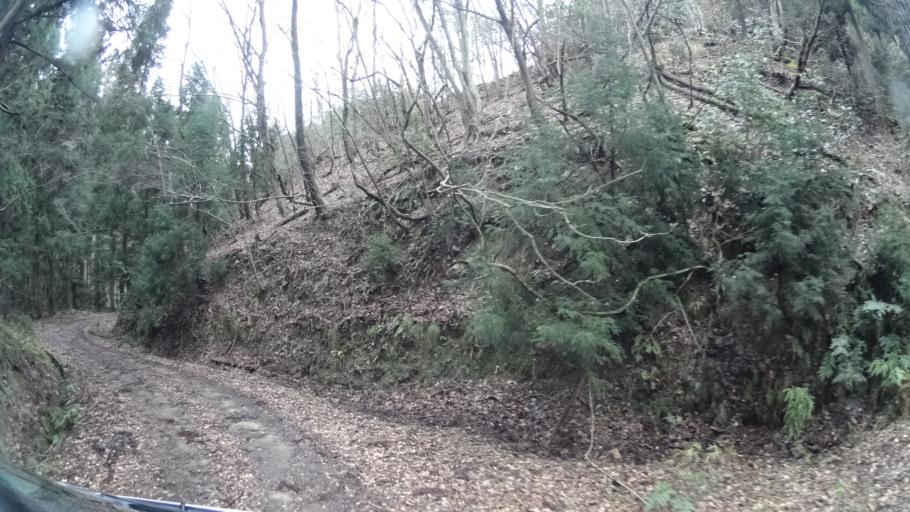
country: JP
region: Kyoto
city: Ayabe
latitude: 35.3133
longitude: 135.3725
